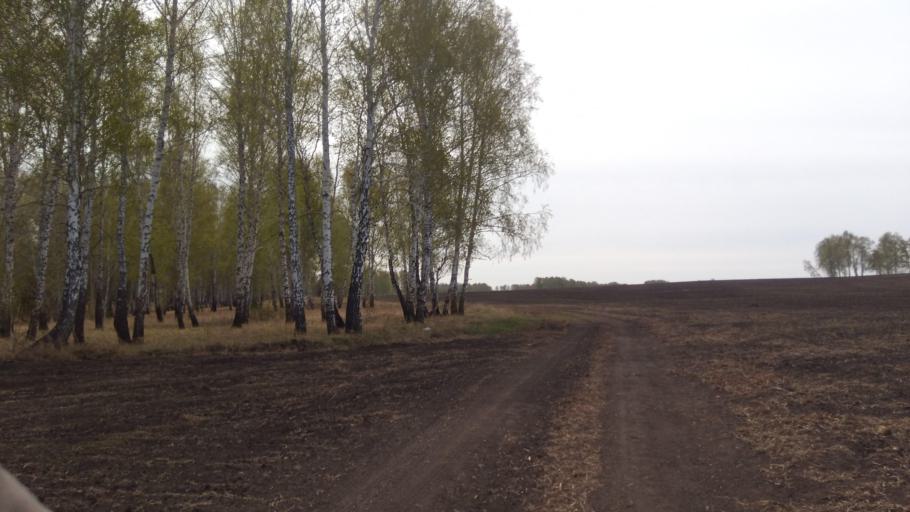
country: RU
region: Chelyabinsk
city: Timiryazevskiy
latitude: 55.0199
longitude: 60.8529
